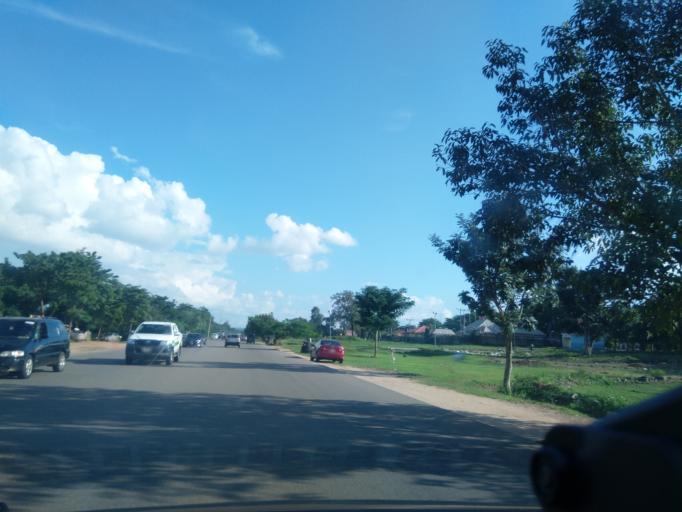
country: NG
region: Abuja Federal Capital Territory
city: Abuja
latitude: 9.0493
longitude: 7.4112
